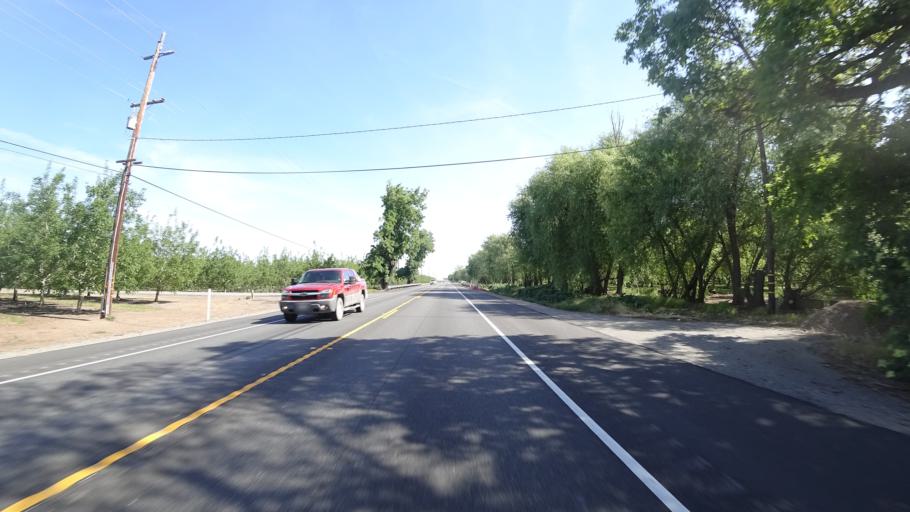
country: US
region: California
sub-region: Glenn County
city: Hamilton City
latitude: 39.8767
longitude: -121.9698
